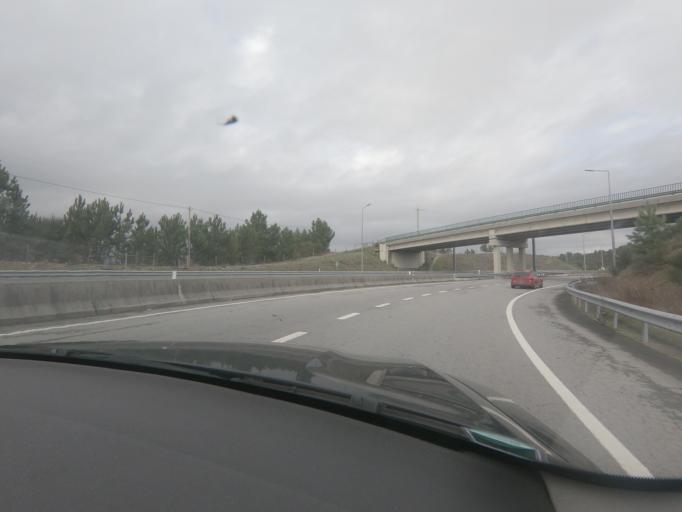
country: PT
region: Vila Real
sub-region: Vila Real
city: Vila Real
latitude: 41.3261
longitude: -7.7011
